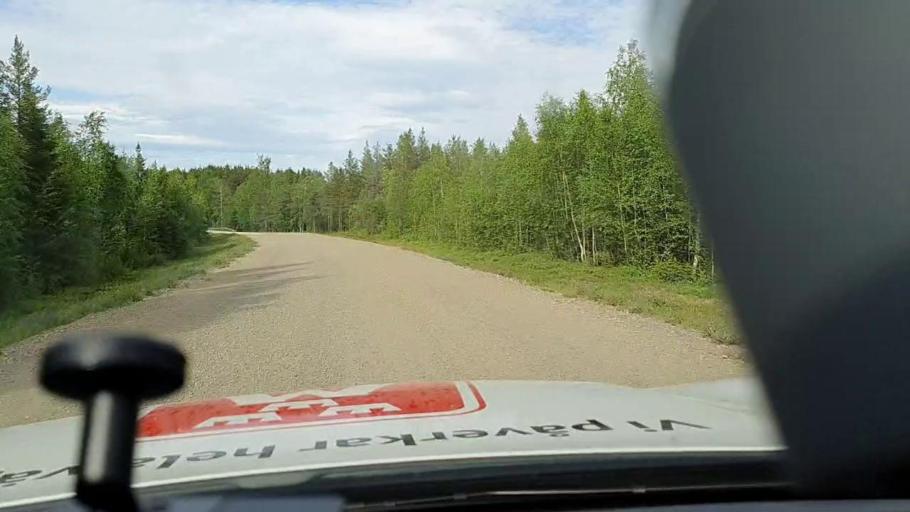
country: SE
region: Norrbotten
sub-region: Alvsbyns Kommun
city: AElvsbyn
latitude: 66.1486
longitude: 21.0287
